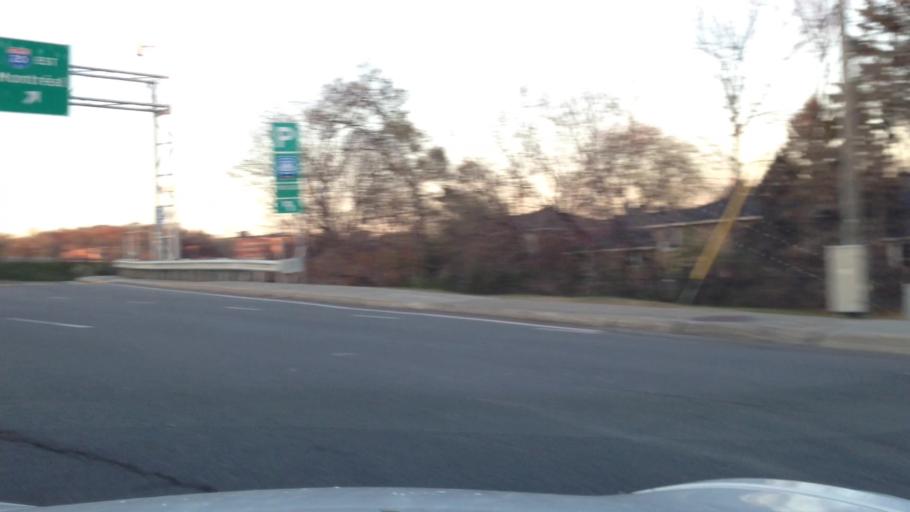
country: CA
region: Quebec
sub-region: Montreal
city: Pointe-Claire
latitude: 45.4413
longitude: -73.8147
